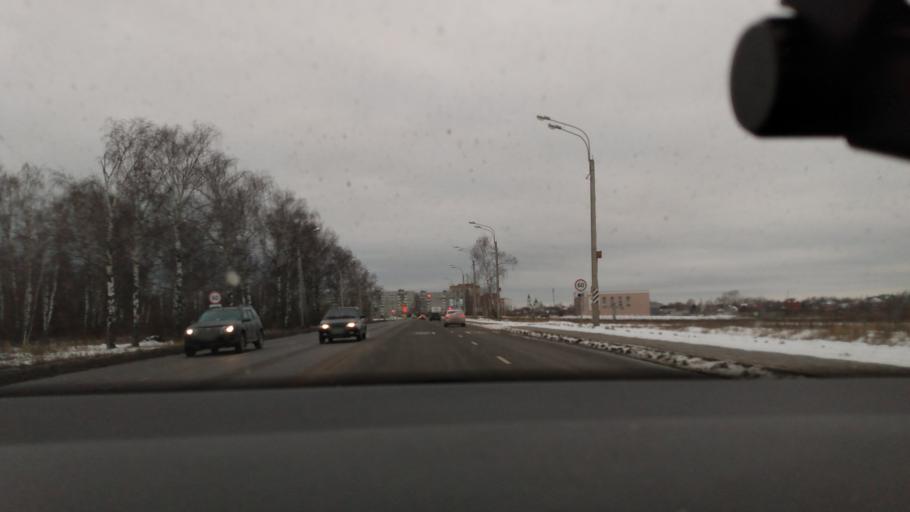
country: RU
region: Moskovskaya
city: Yegor'yevsk
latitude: 55.3845
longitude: 39.0692
